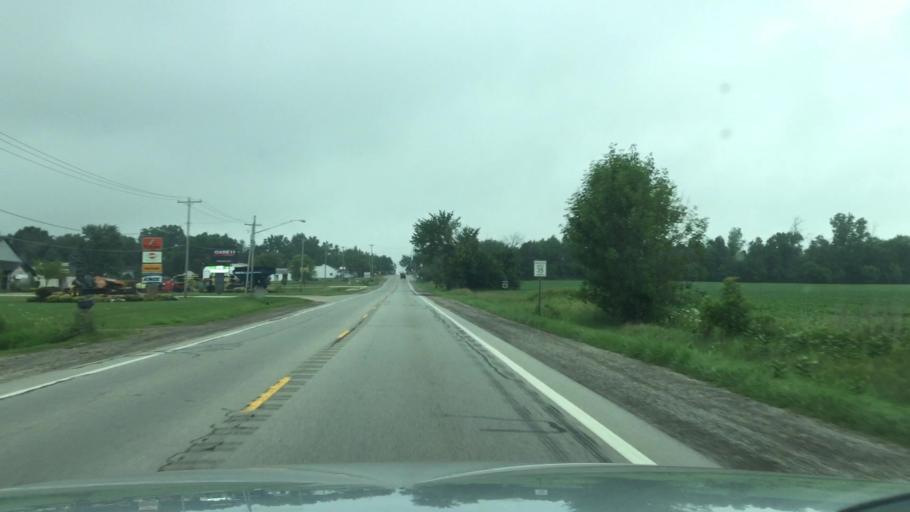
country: US
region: Michigan
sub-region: Shiawassee County
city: Durand
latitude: 42.9789
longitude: -83.9287
